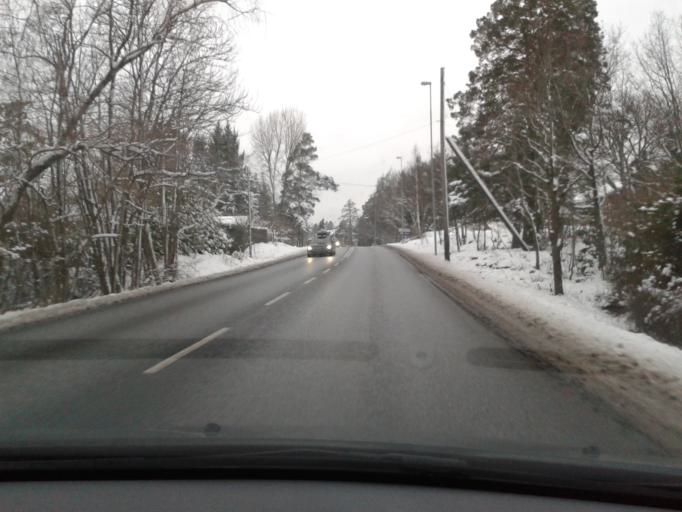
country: SE
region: Stockholm
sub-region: Nacka Kommun
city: Fisksatra
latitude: 59.2437
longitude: 18.2775
